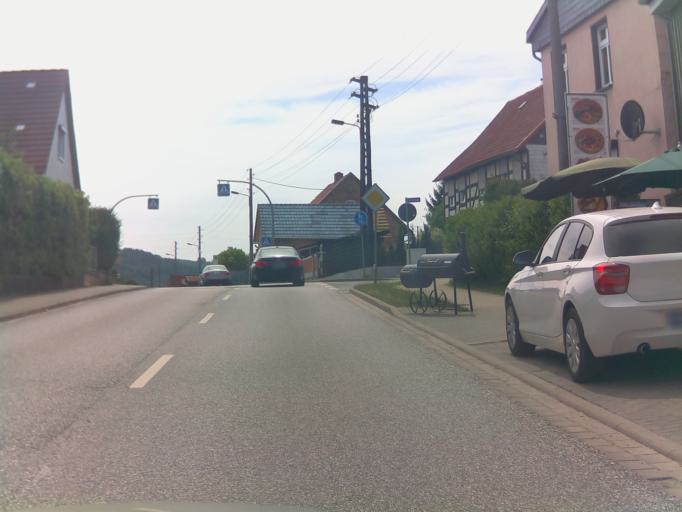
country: DE
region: Saxony-Anhalt
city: Blankenburg
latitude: 51.7764
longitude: 10.9670
